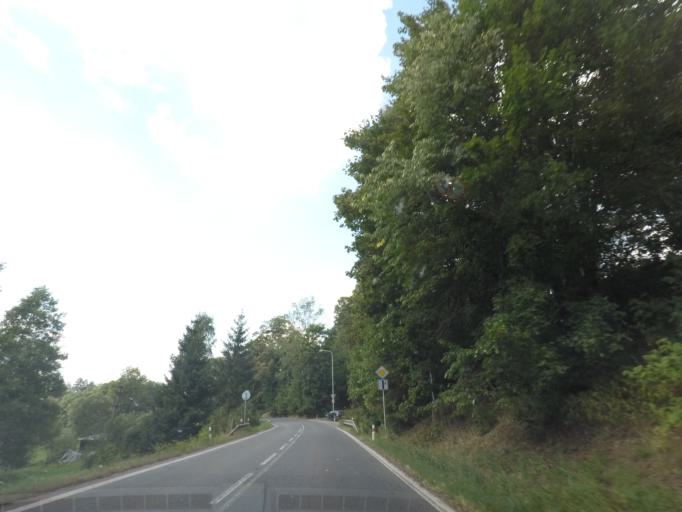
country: CZ
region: Kralovehradecky
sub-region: Okres Trutnov
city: Trutnov
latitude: 50.5587
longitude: 15.8675
